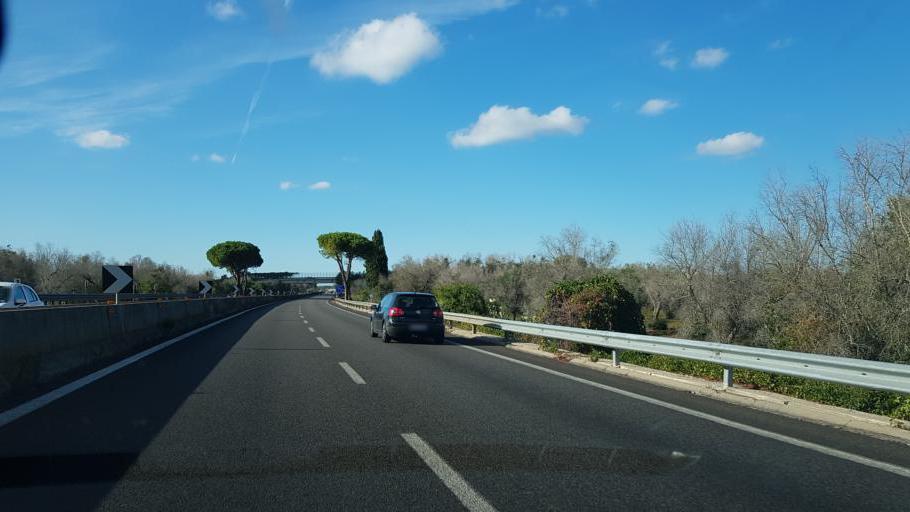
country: IT
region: Apulia
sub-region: Provincia di Lecce
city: Squinzano
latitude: 40.4535
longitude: 18.0650
